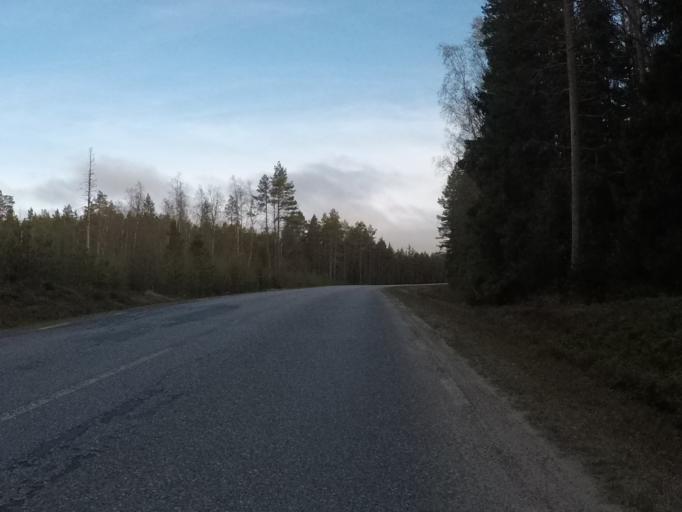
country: SE
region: Vaesterbotten
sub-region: Robertsfors Kommun
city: Robertsfors
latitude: 63.9854
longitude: 20.8121
